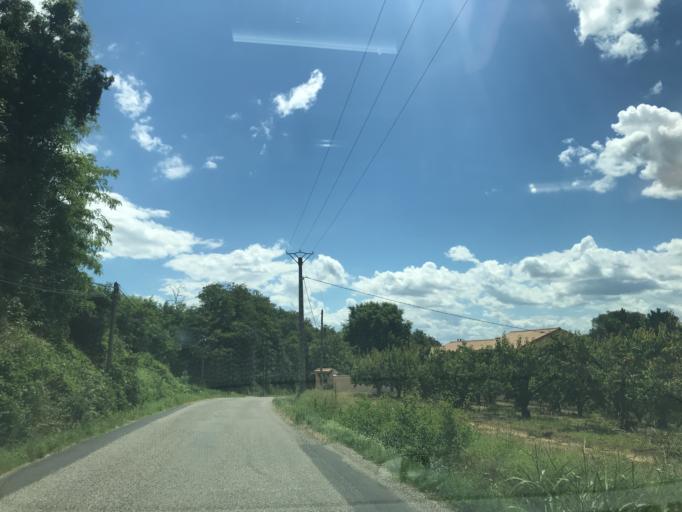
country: FR
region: Rhone-Alpes
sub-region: Departement de la Drome
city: Clerieux
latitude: 45.1287
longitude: 4.9882
